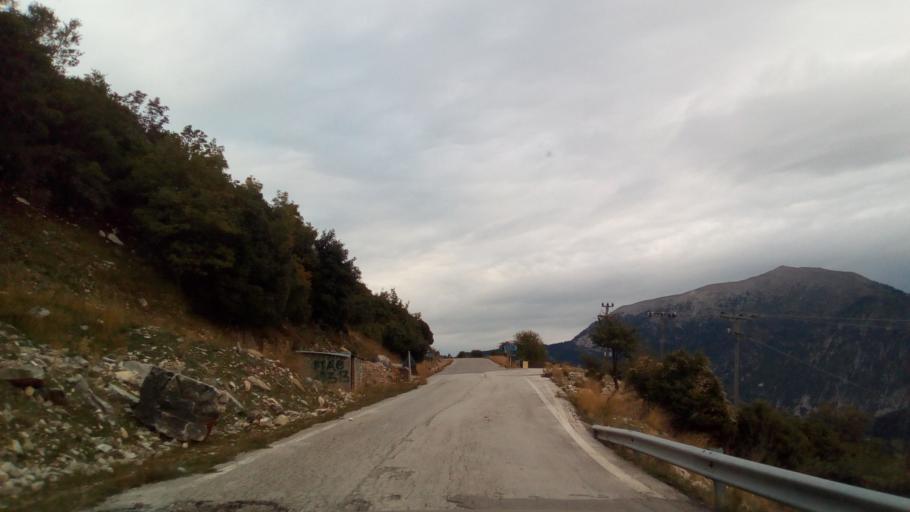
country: GR
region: West Greece
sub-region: Nomos Aitolias kai Akarnanias
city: Thermo
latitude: 38.5928
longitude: 21.8235
